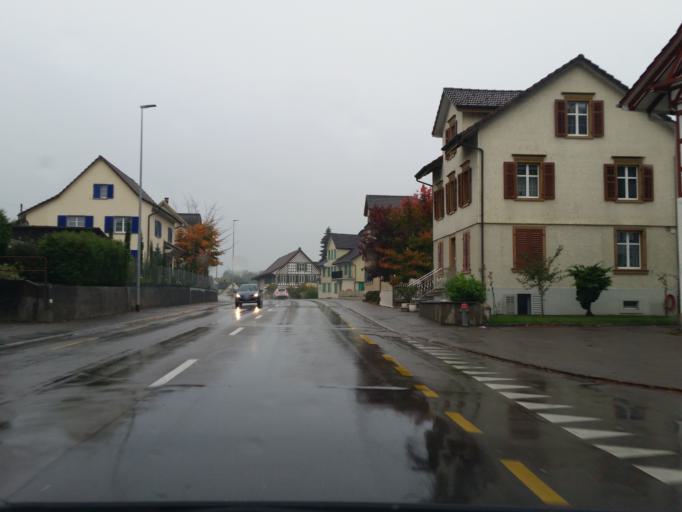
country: CH
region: Thurgau
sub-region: Weinfelden District
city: Erlen
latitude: 47.5456
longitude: 9.2163
